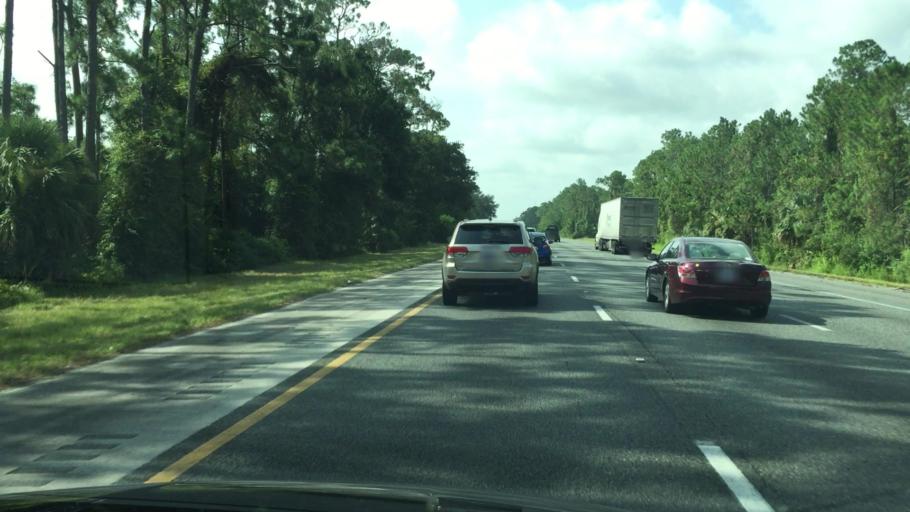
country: US
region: Florida
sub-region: Volusia County
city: Ormond Beach
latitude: 29.2833
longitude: -81.1255
